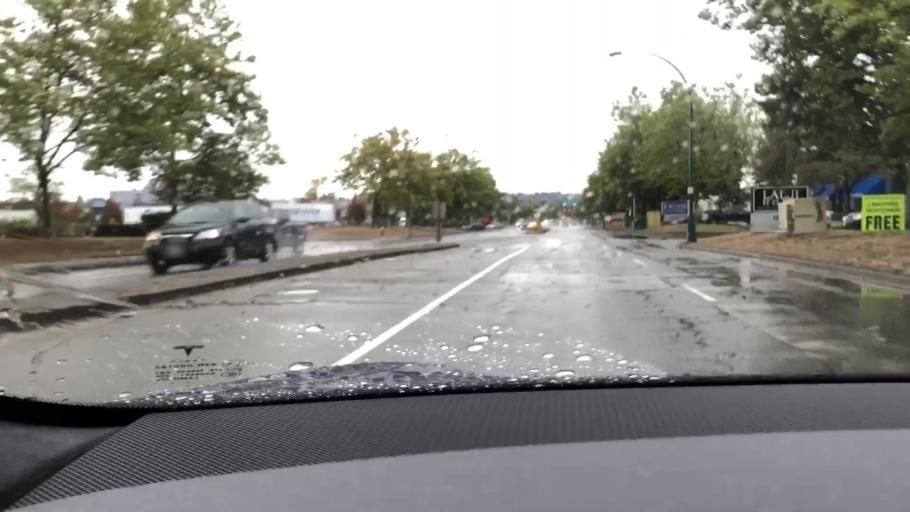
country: CA
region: British Columbia
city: Port Moody
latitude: 49.2287
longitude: -122.8455
